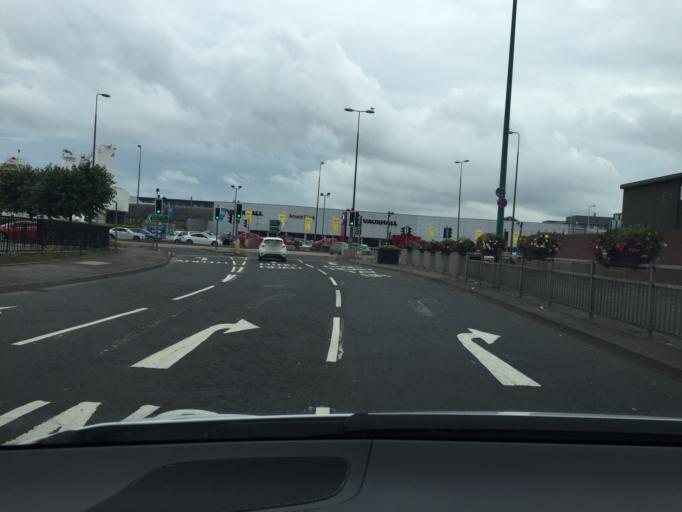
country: GB
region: Scotland
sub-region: Dundee City
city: Dundee
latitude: 56.4631
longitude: -2.9633
